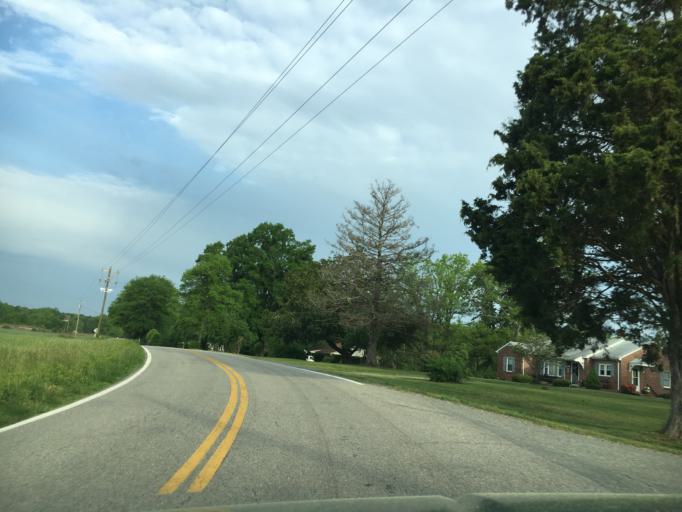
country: US
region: Virginia
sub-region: Halifax County
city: Halifax
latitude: 36.8893
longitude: -78.7969
